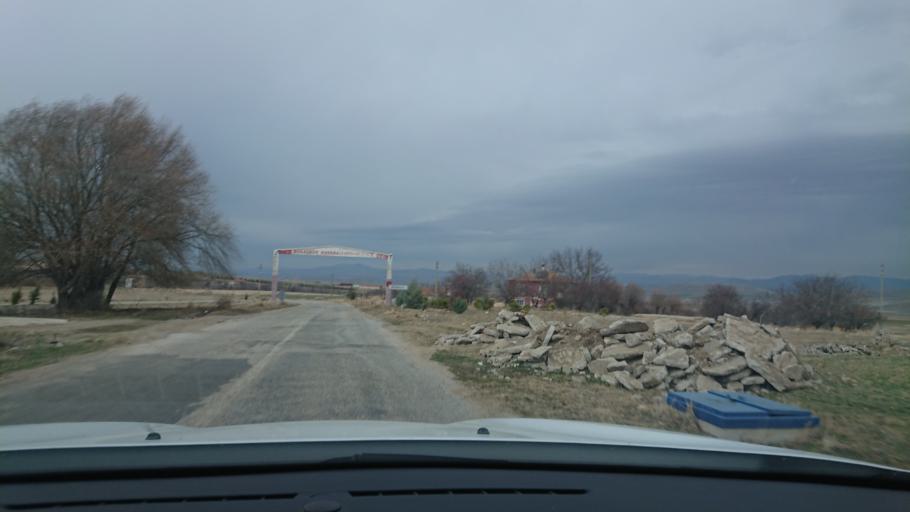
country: TR
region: Aksaray
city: Sariyahsi
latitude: 38.9570
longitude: 33.8945
